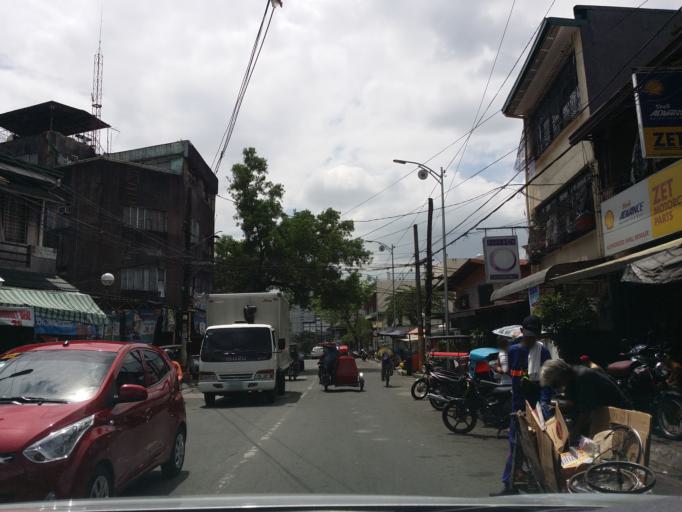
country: PH
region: Metro Manila
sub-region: Mandaluyong
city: Mandaluyong City
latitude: 14.5788
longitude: 121.0130
